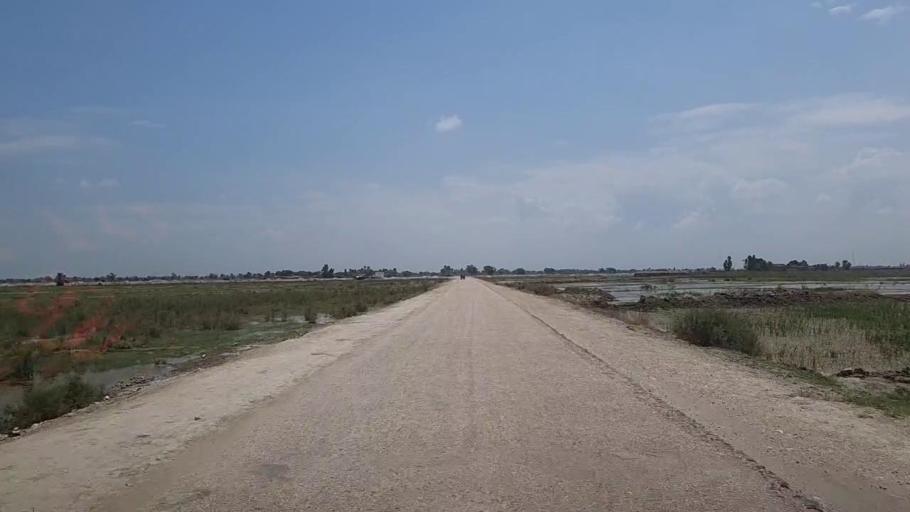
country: PK
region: Sindh
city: Kandhkot
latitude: 28.2791
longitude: 69.1745
